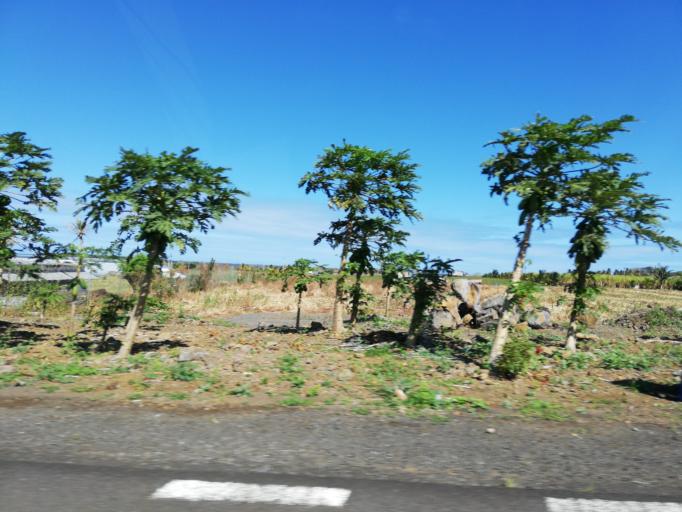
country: MU
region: Grand Port
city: Plaine Magnien
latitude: -20.4442
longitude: 57.6835
